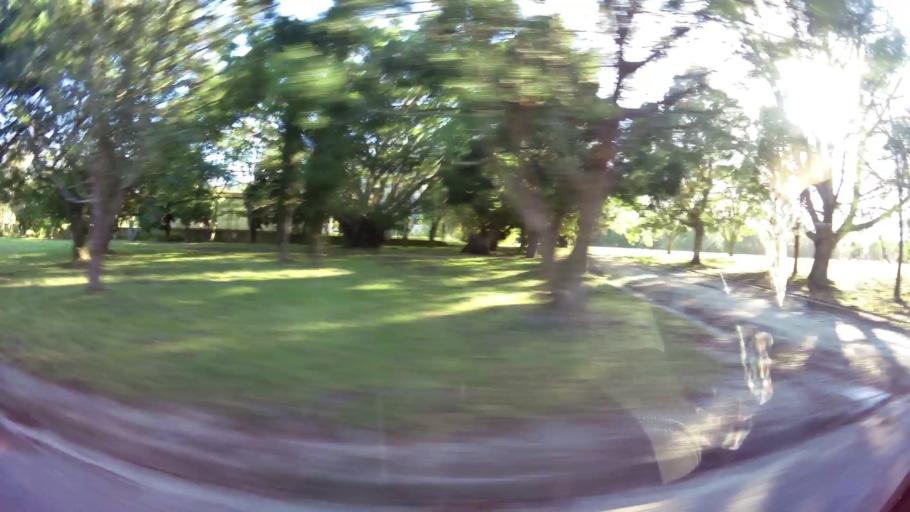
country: ZA
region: Western Cape
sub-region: Eden District Municipality
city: George
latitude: -33.9471
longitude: 22.4523
